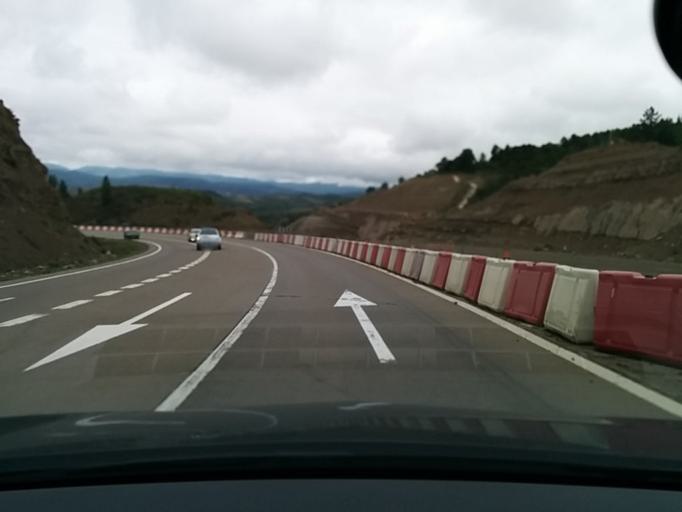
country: ES
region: Aragon
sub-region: Provincia de Huesca
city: Arguis
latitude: 42.3949
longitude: -0.3713
